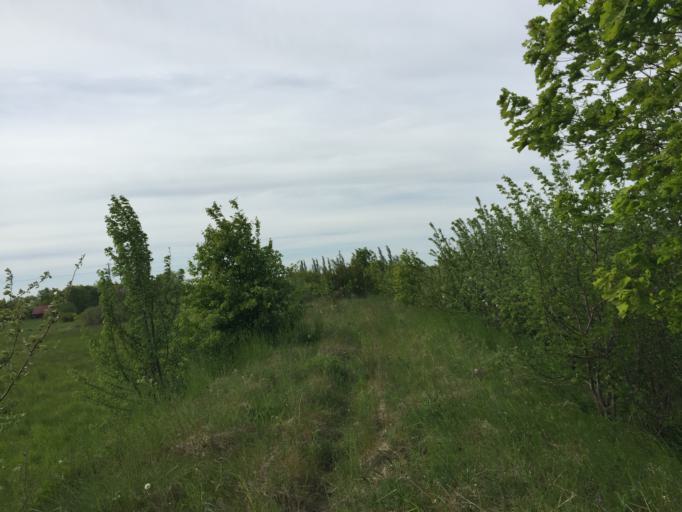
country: LT
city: Linkuva
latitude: 56.0256
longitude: 24.1844
